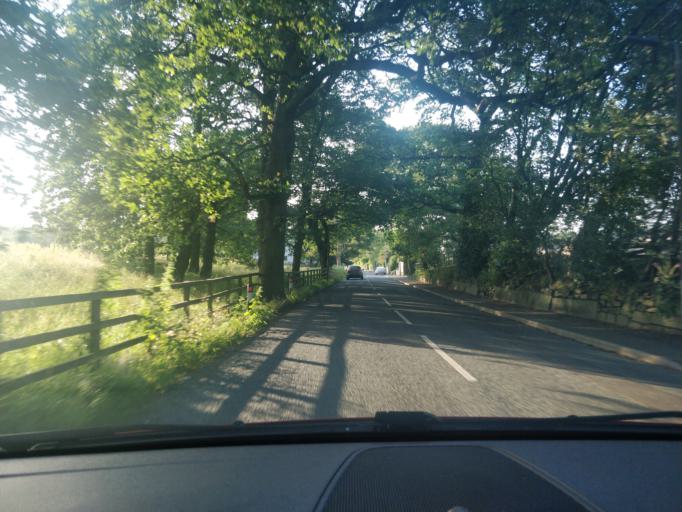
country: GB
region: England
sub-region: Lancashire
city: Parbold
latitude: 53.5721
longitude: -2.7644
